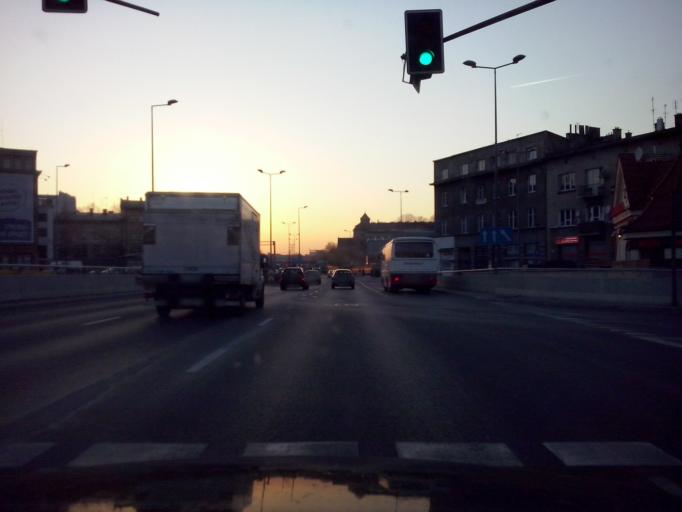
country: PL
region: Lesser Poland Voivodeship
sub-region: Krakow
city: Krakow
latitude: 50.0666
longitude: 19.9595
